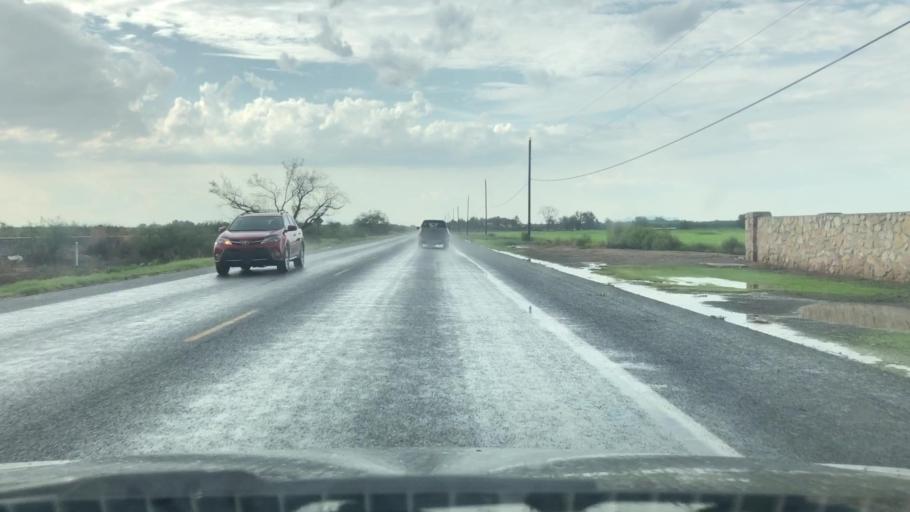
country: US
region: New Mexico
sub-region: Dona Ana County
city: Mesquite
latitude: 32.1830
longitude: -106.7081
